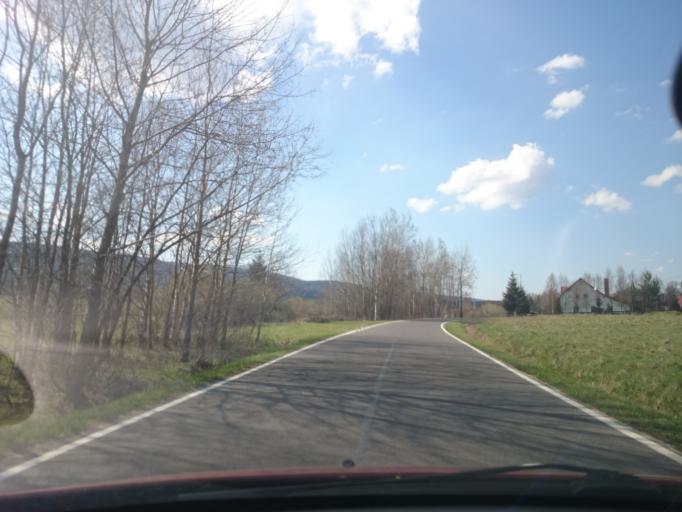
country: PL
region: Lower Silesian Voivodeship
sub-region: Powiat klodzki
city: Szczytna
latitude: 50.3003
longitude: 16.4567
